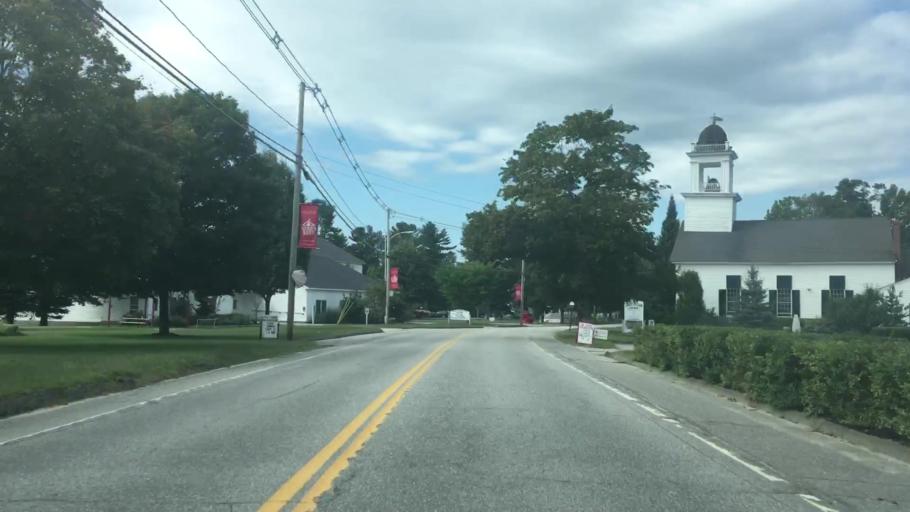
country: US
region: Maine
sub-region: Cumberland County
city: Raymond
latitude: 44.0038
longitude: -70.5220
